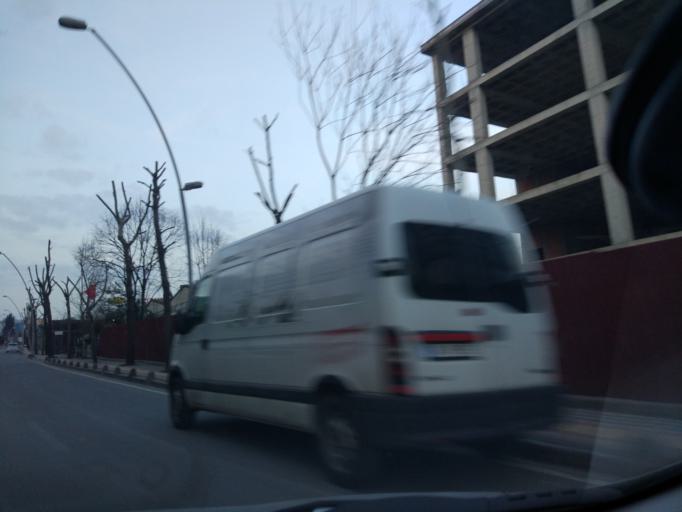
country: TR
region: Istanbul
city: Bahcelievler
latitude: 41.0028
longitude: 28.8219
